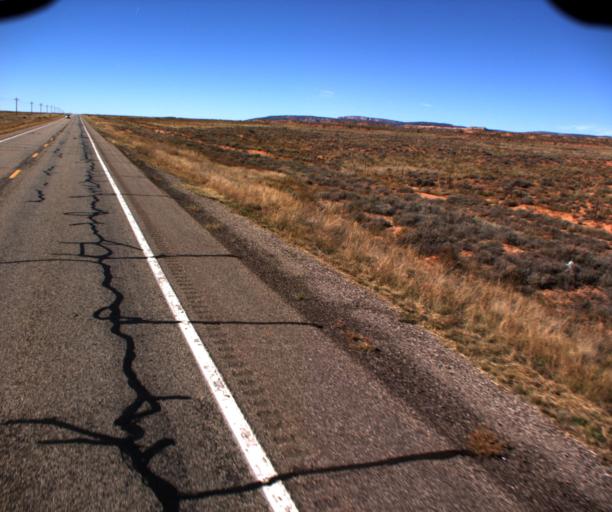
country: US
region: Arizona
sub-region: Coconino County
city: Fredonia
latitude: 36.8933
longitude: -112.6151
